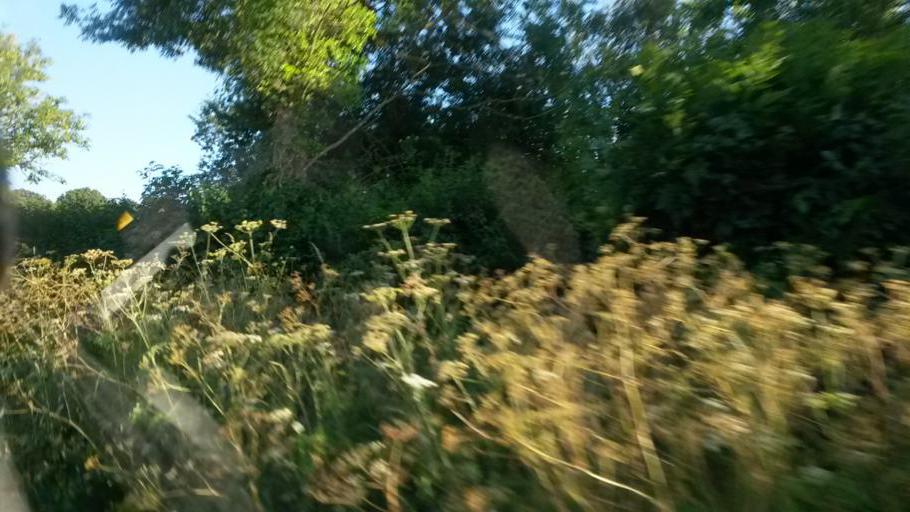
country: IE
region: Leinster
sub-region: An Mhi
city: Ashbourne
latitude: 53.4779
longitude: -6.3270
